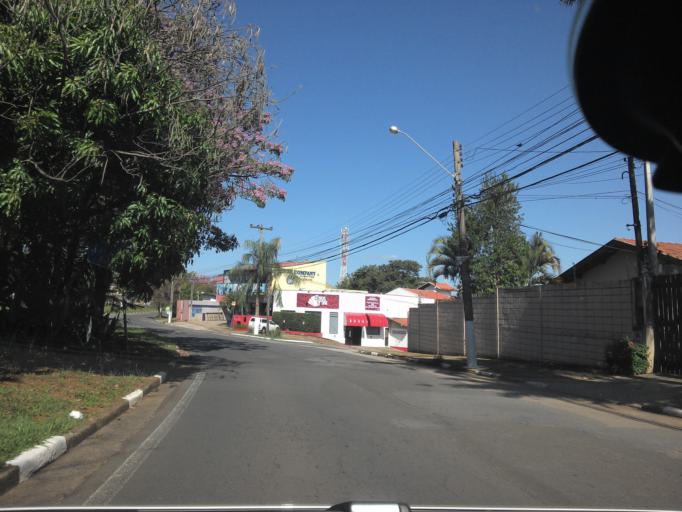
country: BR
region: Sao Paulo
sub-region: Campinas
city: Campinas
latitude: -22.8357
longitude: -47.0560
